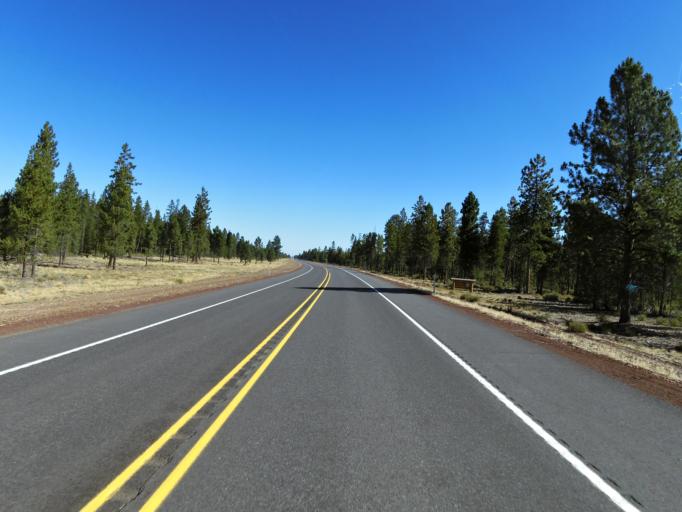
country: US
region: Oregon
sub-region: Deschutes County
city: La Pine
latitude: 43.5472
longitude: -121.6049
